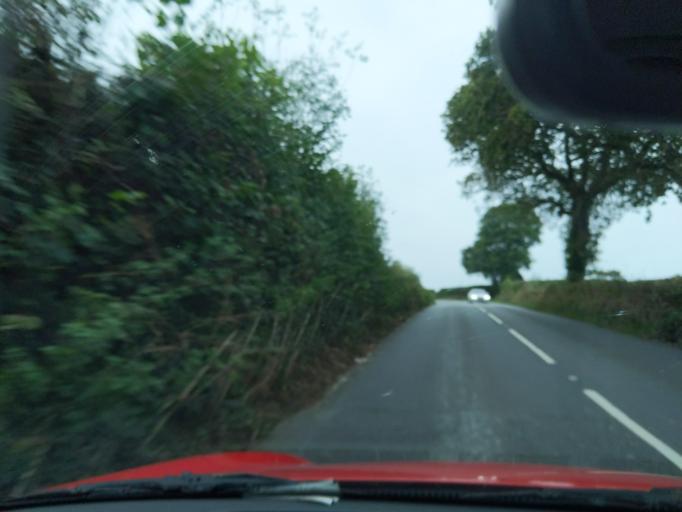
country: GB
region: England
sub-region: Devon
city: Okehampton
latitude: 50.8412
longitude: -4.0782
